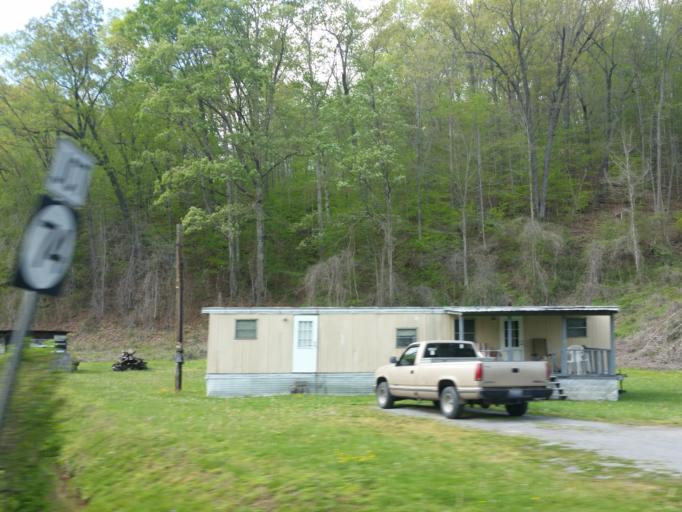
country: US
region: Kentucky
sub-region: Bell County
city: Middlesboro
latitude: 36.6157
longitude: -83.7641
